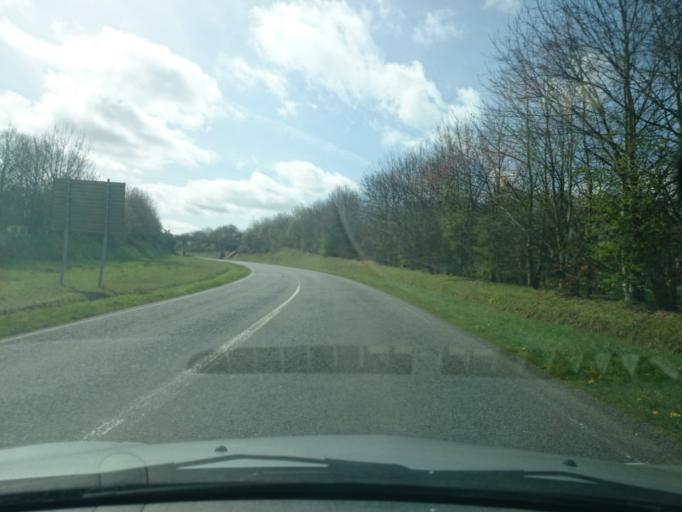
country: FR
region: Brittany
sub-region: Departement du Finistere
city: Gouesnou
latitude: 48.4425
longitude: -4.4576
